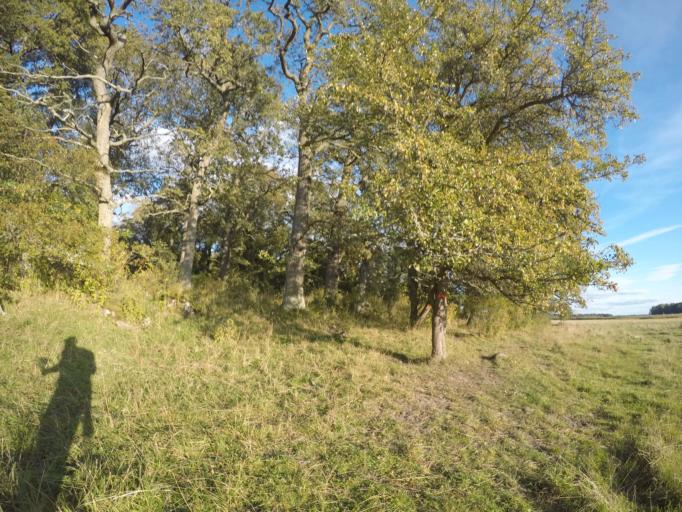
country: SE
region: Vaestmanland
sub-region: Hallstahammars Kommun
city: Kolback
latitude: 59.4775
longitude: 16.2232
